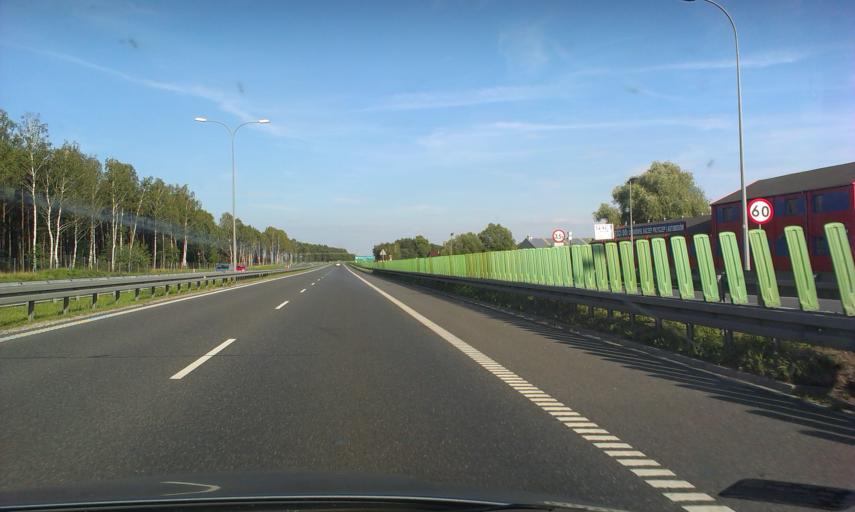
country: PL
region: Kujawsko-Pomorskie
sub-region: Powiat bydgoski
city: Biale Blota
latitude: 53.0651
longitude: 17.9432
